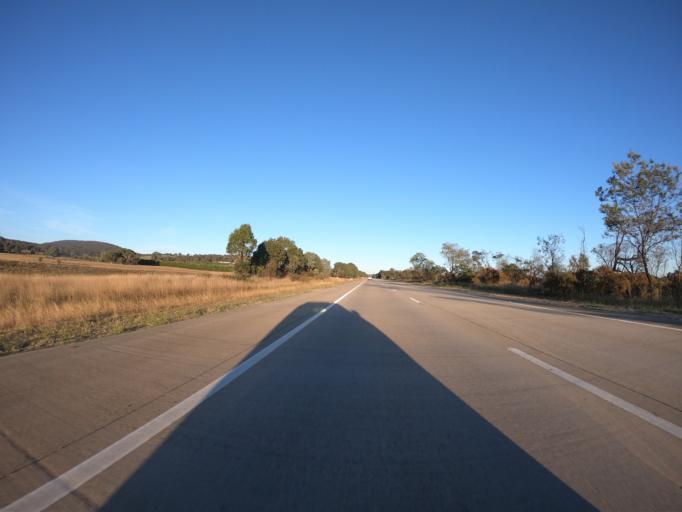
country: AU
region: New South Wales
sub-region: Yass Valley
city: Gundaroo
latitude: -34.9011
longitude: 149.4703
